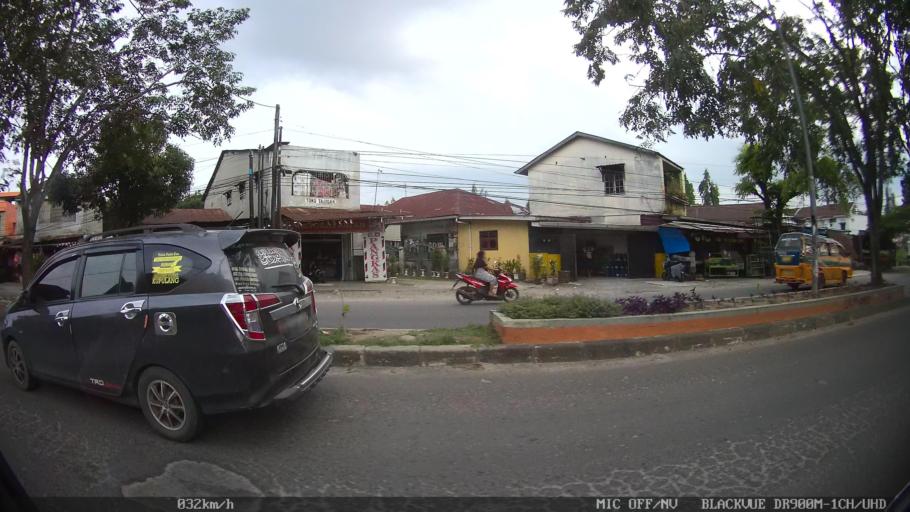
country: ID
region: North Sumatra
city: Sunggal
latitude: 3.5502
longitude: 98.6090
